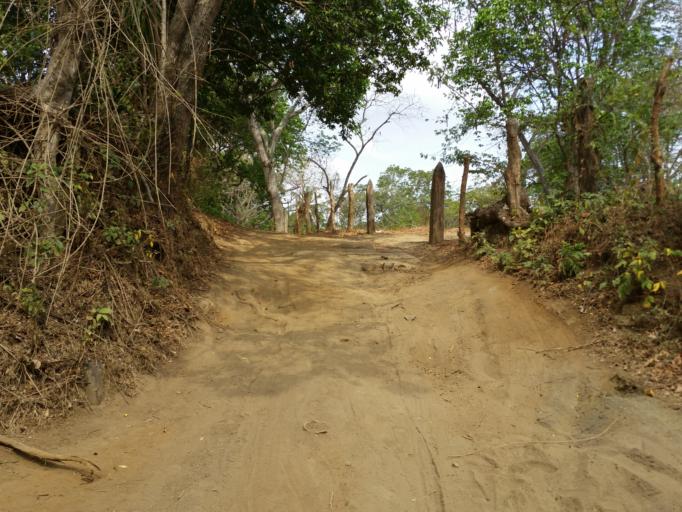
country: NI
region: Masaya
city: Ticuantepe
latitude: 12.0696
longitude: -86.2462
